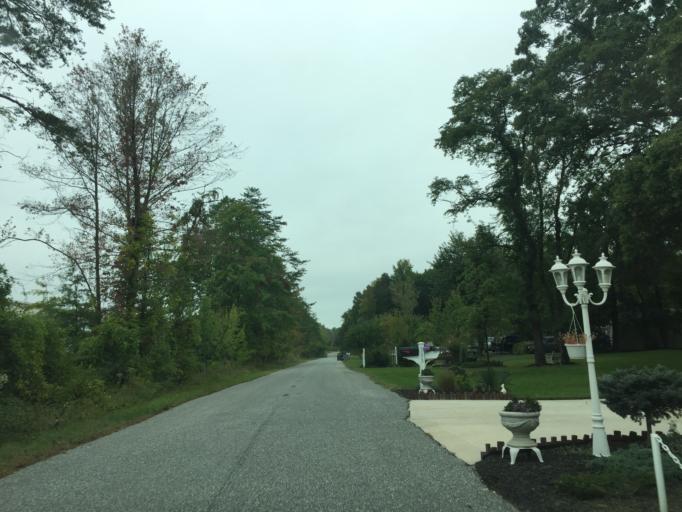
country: US
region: Maryland
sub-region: Baltimore County
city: Bowleys Quarters
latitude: 39.3461
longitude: -76.4018
